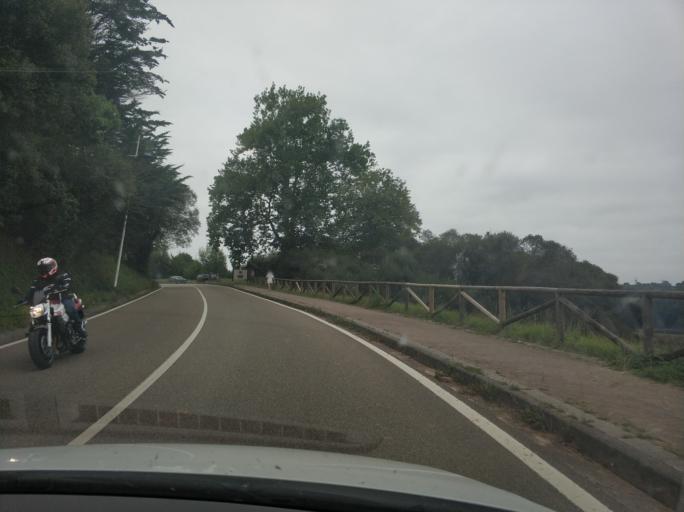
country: ES
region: Cantabria
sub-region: Provincia de Cantabria
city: Comillas
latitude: 43.3813
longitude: -4.3182
